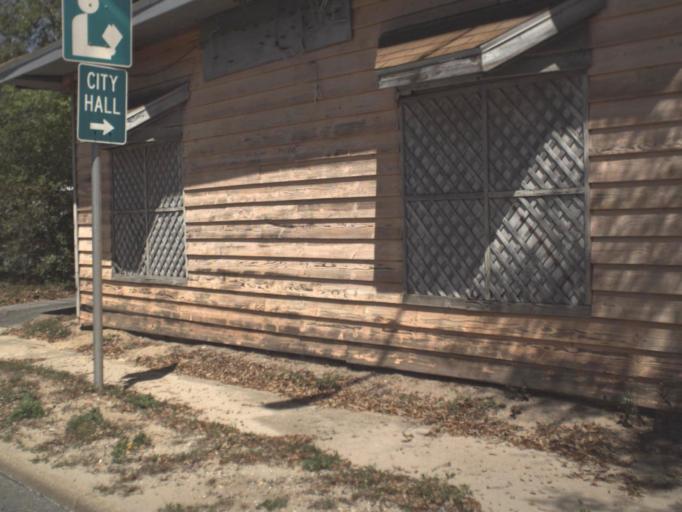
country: US
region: Florida
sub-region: Okaloosa County
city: Mary Esther
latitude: 30.4097
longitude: -86.6626
